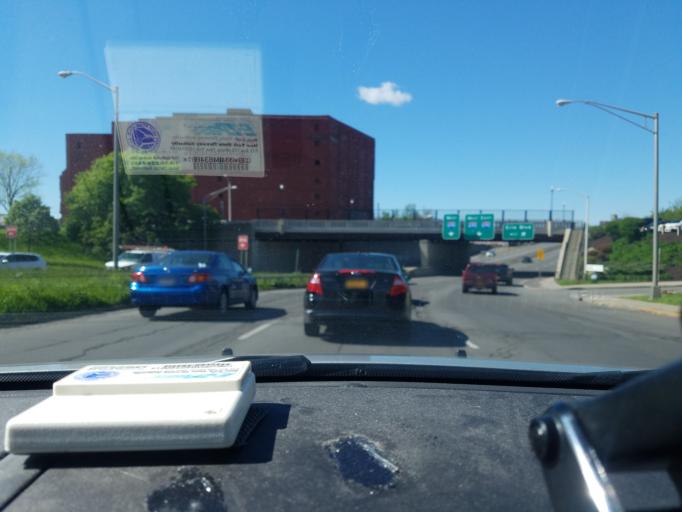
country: US
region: New York
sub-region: Onondaga County
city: Syracuse
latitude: 43.0497
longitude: -76.1588
